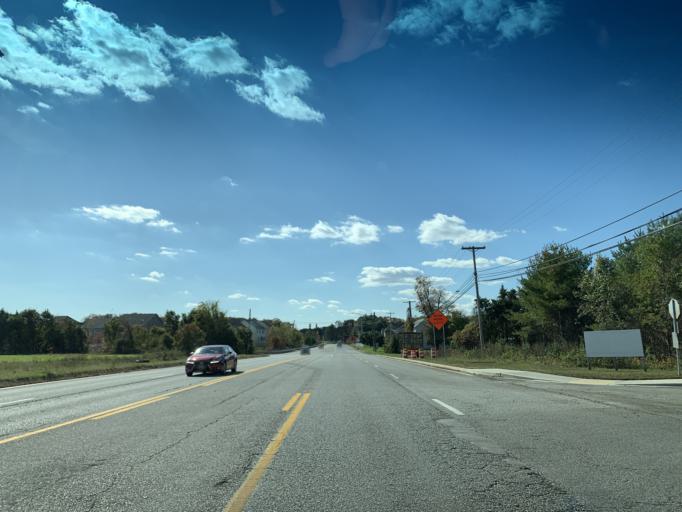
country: US
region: Maryland
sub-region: Anne Arundel County
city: South Gate
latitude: 39.1230
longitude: -76.6442
